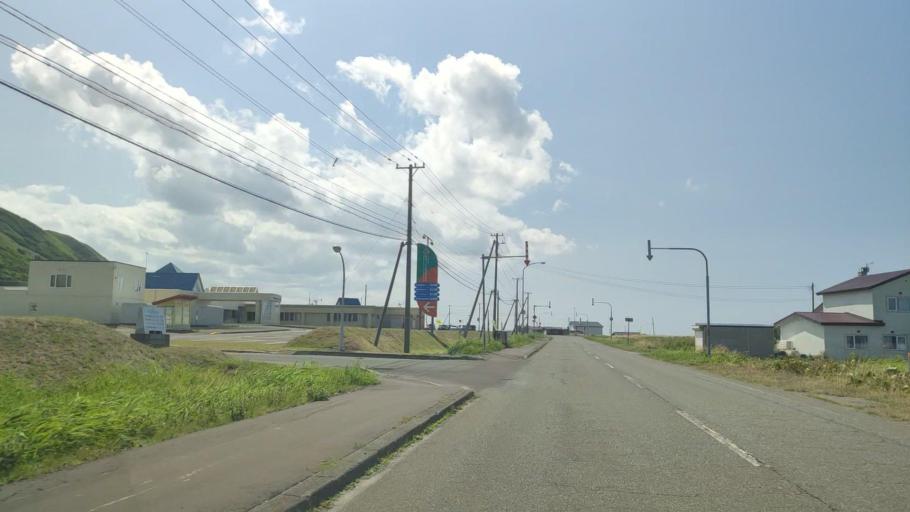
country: JP
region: Hokkaido
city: Wakkanai
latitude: 45.4149
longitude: 141.6366
